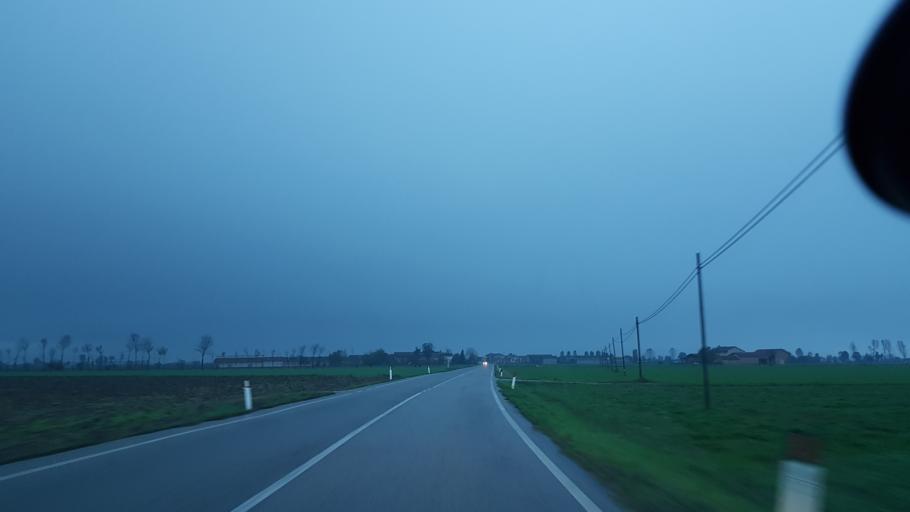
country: IT
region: Piedmont
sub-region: Provincia di Cuneo
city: Fossano
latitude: 44.5578
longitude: 7.6832
